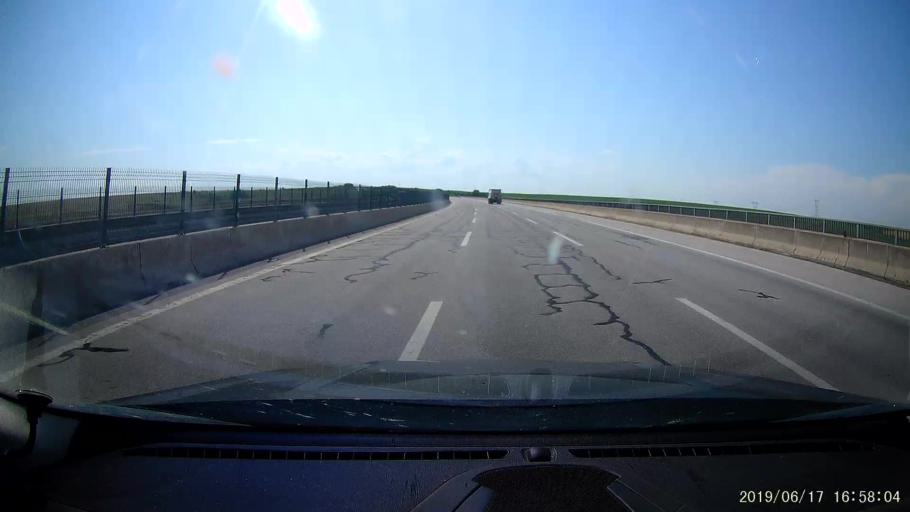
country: TR
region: Edirne
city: Haskoy
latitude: 41.6096
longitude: 26.8988
